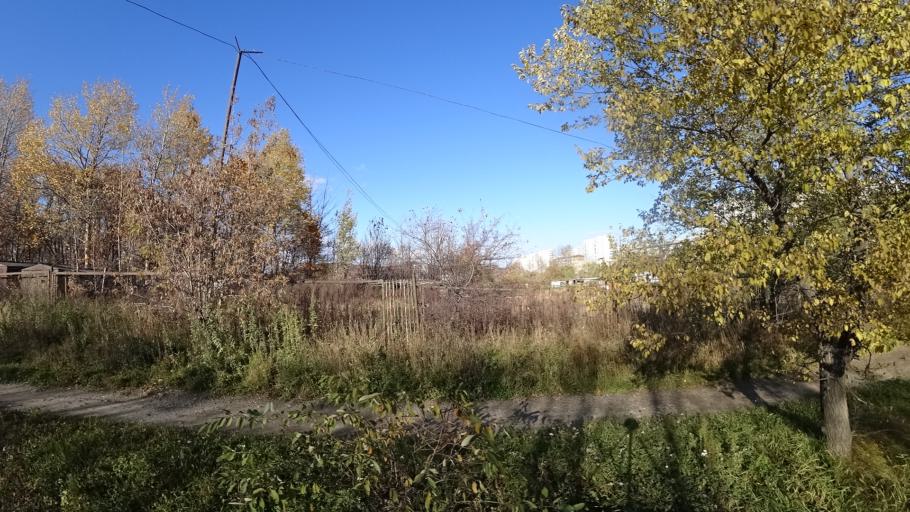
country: RU
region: Khabarovsk Krai
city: Amursk
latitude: 50.2432
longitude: 136.9135
